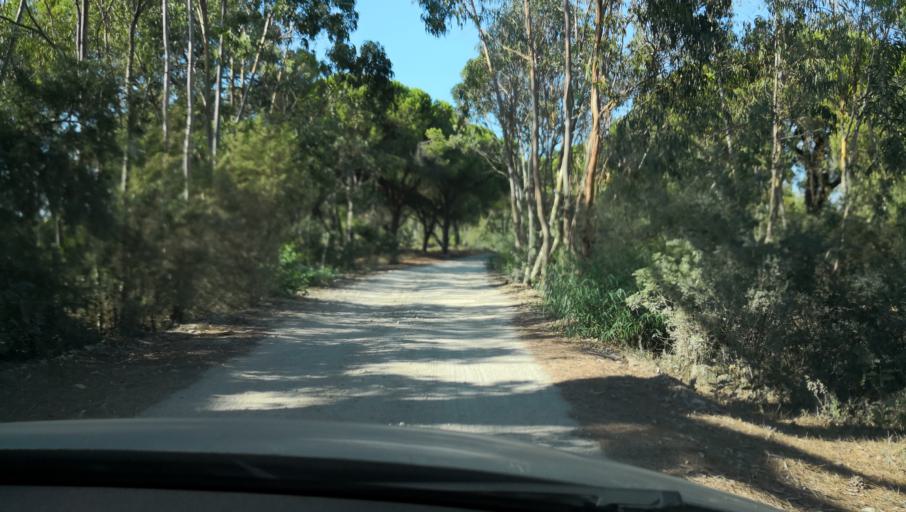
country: PT
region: Setubal
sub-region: Setubal
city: Setubal
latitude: 38.4759
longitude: -8.8795
